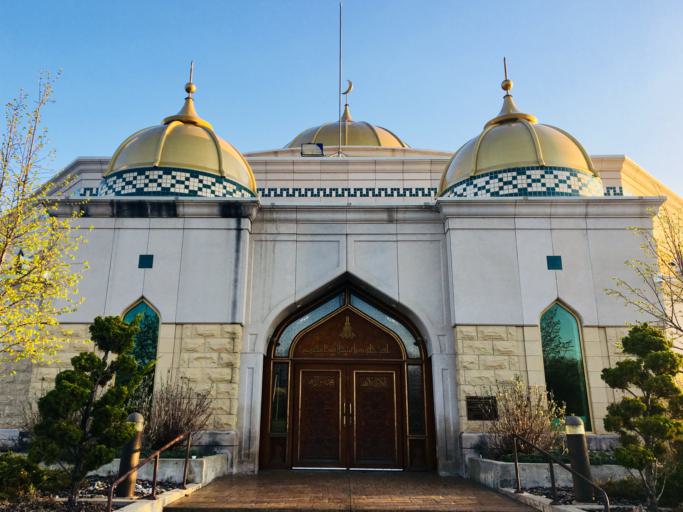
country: US
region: Michigan
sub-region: Wayne County
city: Dearborn Heights
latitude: 42.3299
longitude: -83.2297
